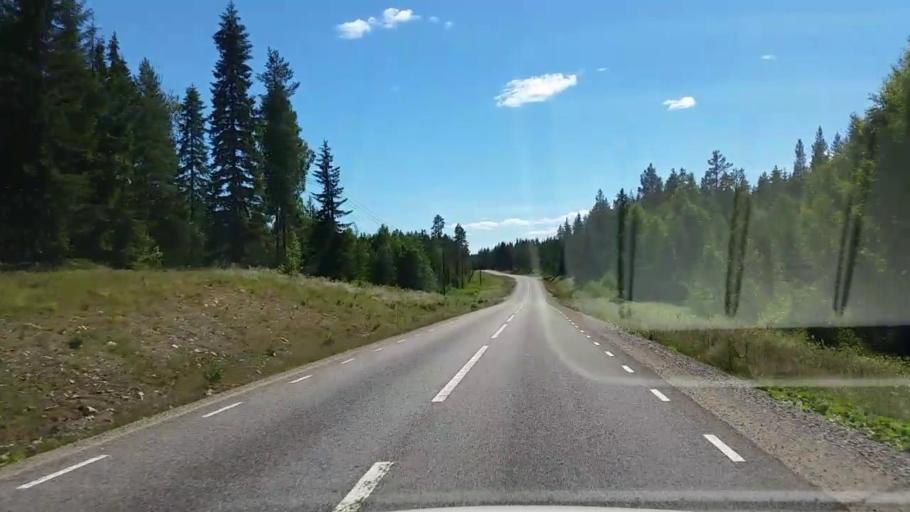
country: SE
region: Gaevleborg
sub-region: Ovanakers Kommun
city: Edsbyn
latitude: 61.5091
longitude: 15.6828
